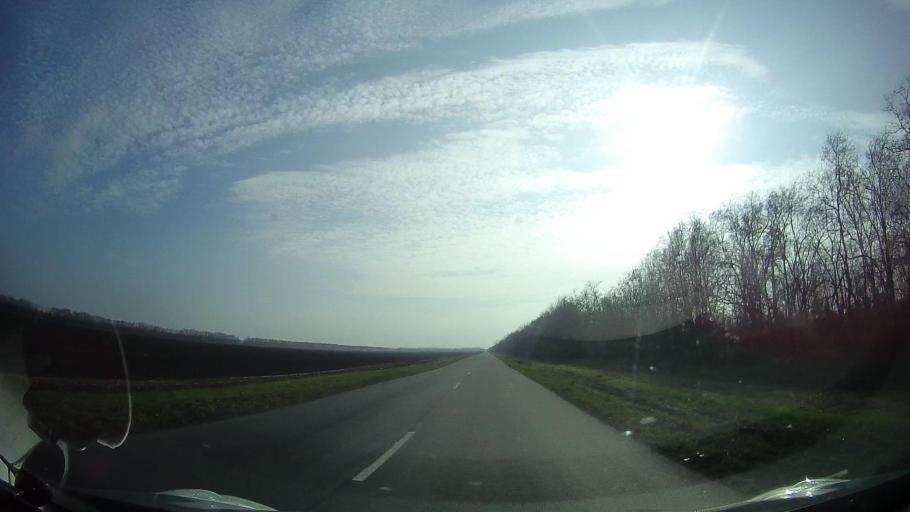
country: RU
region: Rostov
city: Mechetinskaya
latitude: 46.8860
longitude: 40.5419
